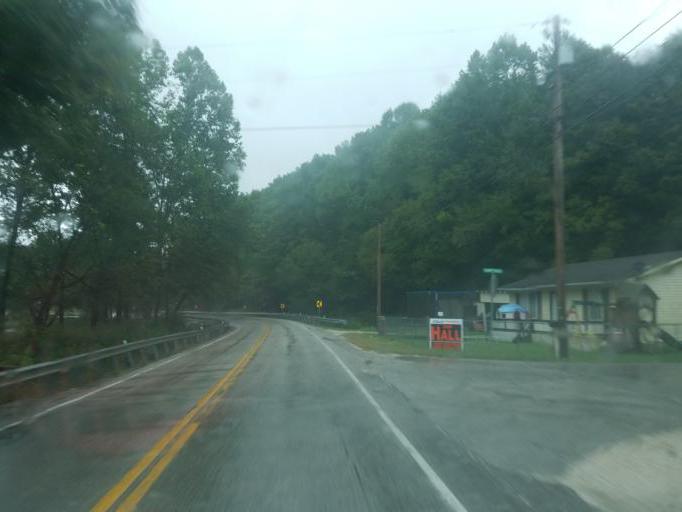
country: US
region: Kentucky
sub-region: Rowan County
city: Morehead
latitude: 38.2575
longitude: -83.3335
